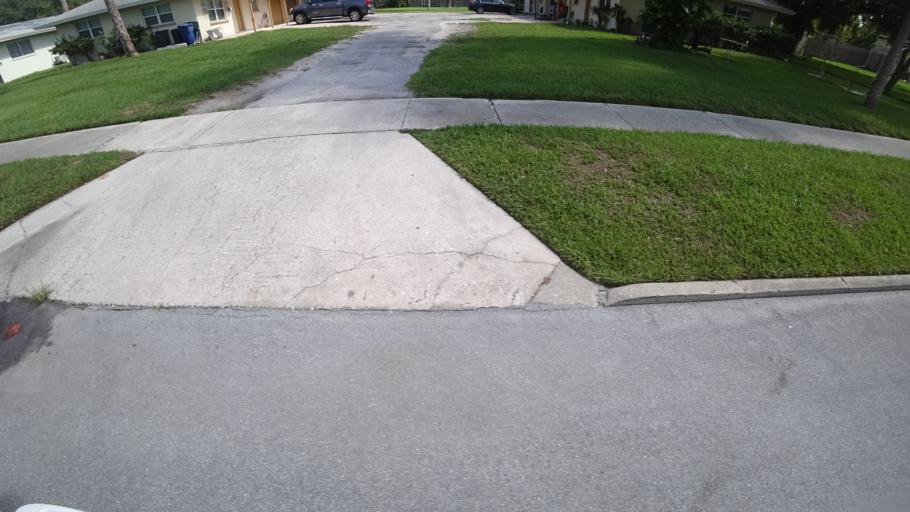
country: US
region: Florida
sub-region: Manatee County
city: Whitfield
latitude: 27.3965
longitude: -82.5656
